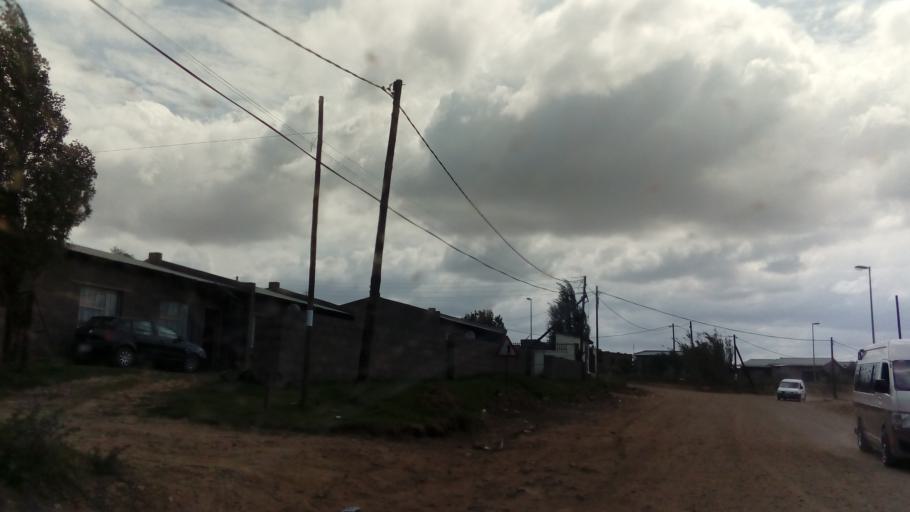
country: LS
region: Maseru
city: Maseru
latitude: -29.3712
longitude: 27.5325
